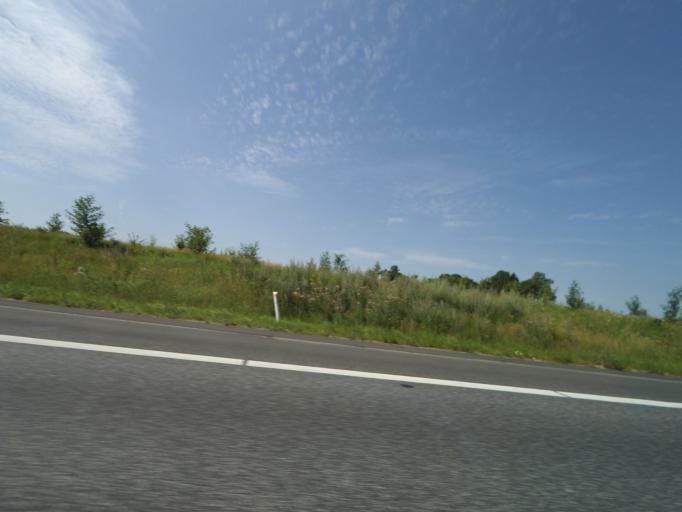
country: DK
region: South Denmark
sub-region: Vejle Kommune
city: Borkop
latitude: 55.6137
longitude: 9.5804
